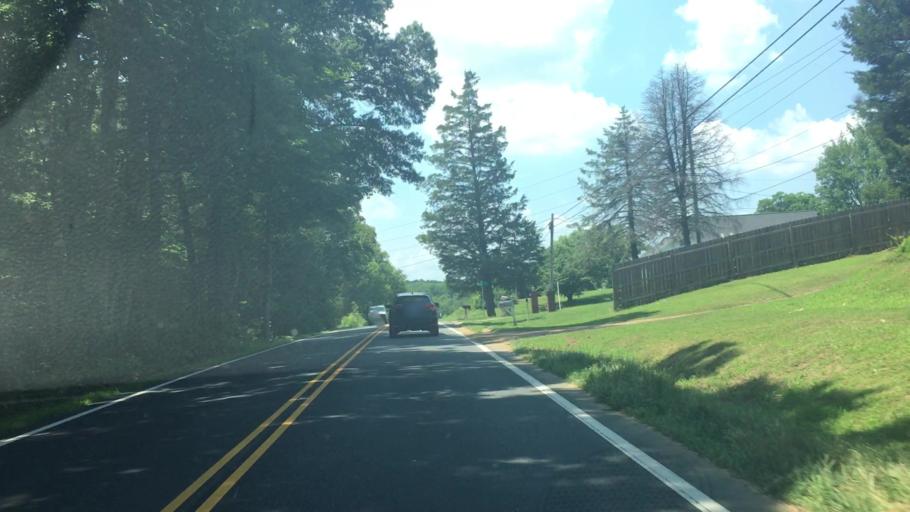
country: US
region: Virginia
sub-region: King George County
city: Passapatanzy
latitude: 38.3028
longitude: -77.3846
